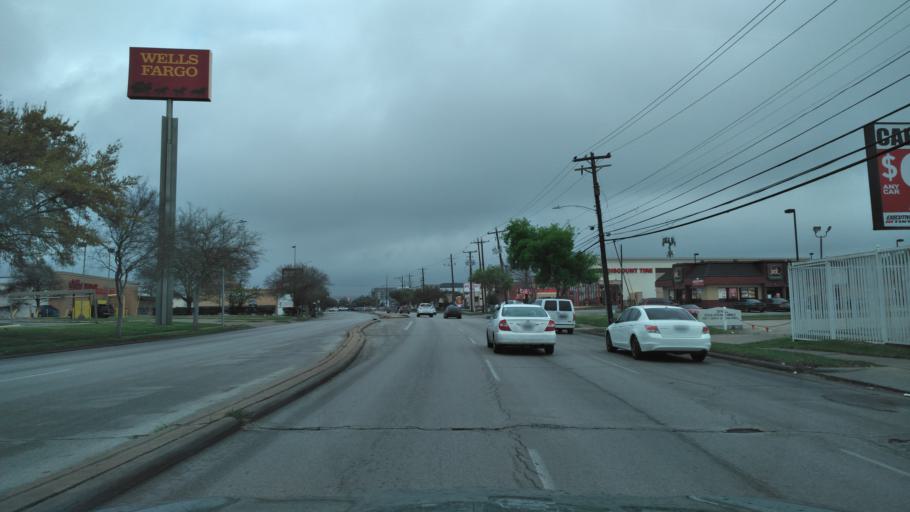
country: US
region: Texas
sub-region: Harris County
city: Piney Point Village
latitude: 29.7351
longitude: -95.5010
